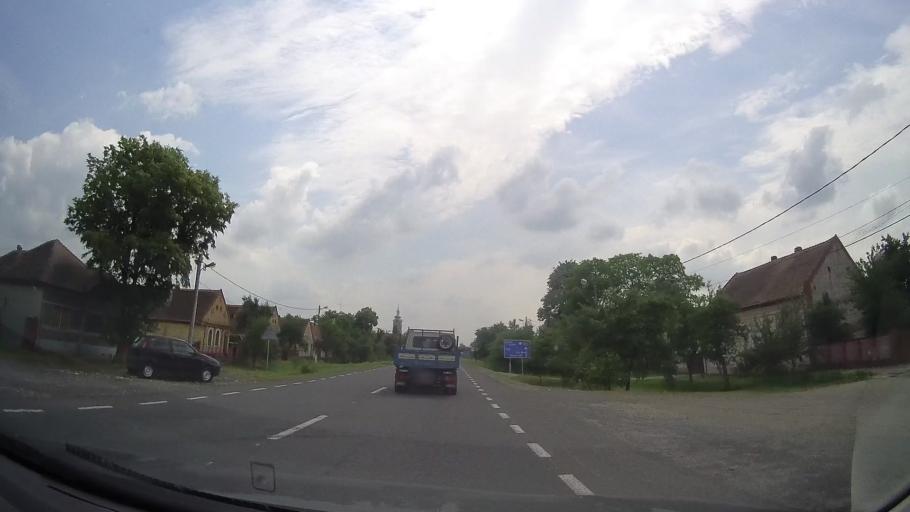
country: RO
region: Timis
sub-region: Comuna Topolovatu Mare
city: Topolovatu Mare
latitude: 45.7889
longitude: 21.5799
